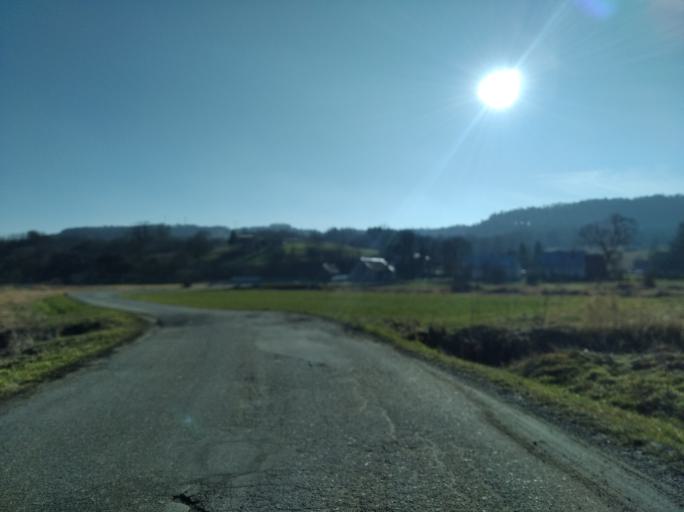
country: PL
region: Subcarpathian Voivodeship
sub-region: Powiat brzozowski
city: Domaradz
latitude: 49.8021
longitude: 21.9071
